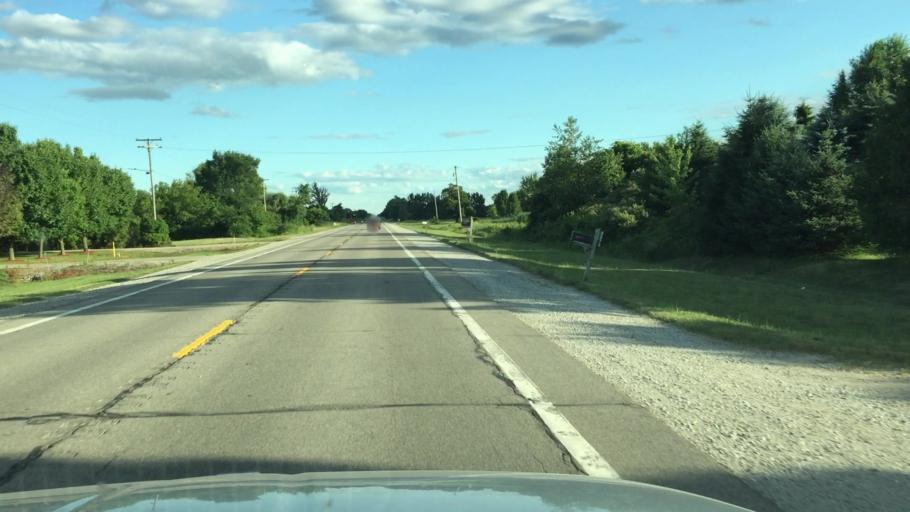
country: US
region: Michigan
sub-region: Saint Clair County
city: Yale
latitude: 43.0561
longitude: -82.7642
